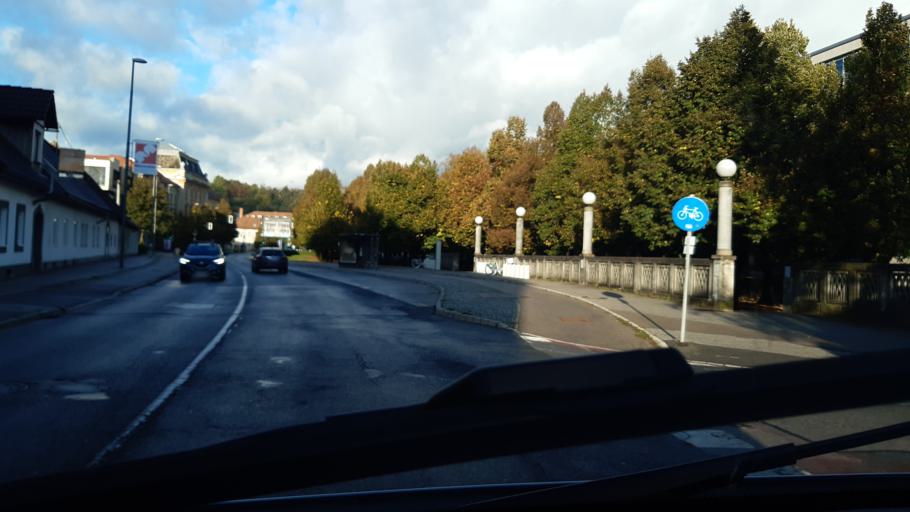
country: SI
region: Ljubljana
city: Ljubljana
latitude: 46.0490
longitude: 14.5236
